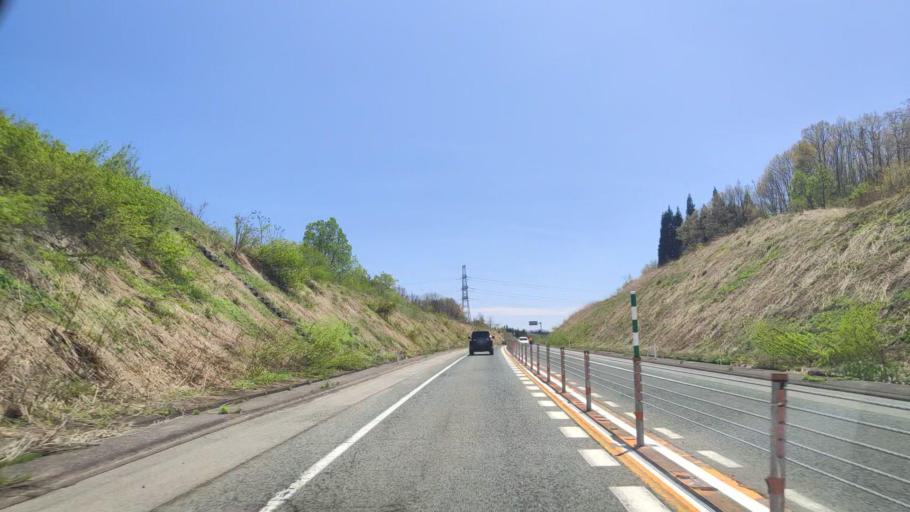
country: JP
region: Yamagata
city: Shinjo
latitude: 38.7210
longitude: 140.3087
